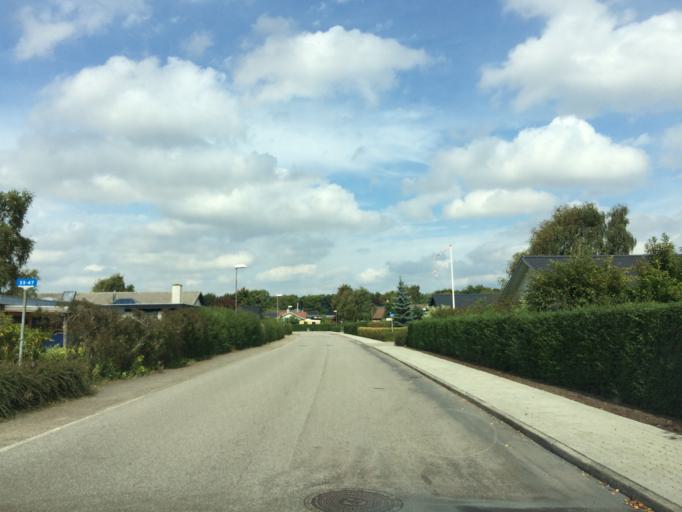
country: DK
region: Central Jutland
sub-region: Holstebro Kommune
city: Holstebro
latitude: 56.3791
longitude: 8.5953
